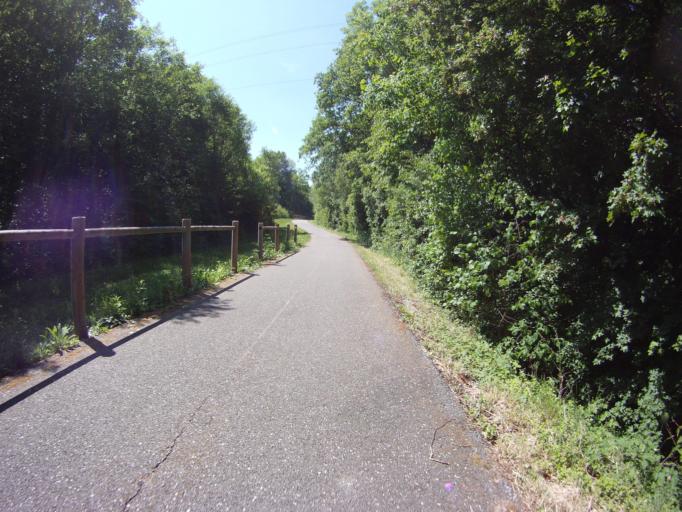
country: FR
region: Lorraine
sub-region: Departement de Meurthe-et-Moselle
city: Champenoux
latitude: 48.7458
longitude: 6.3208
